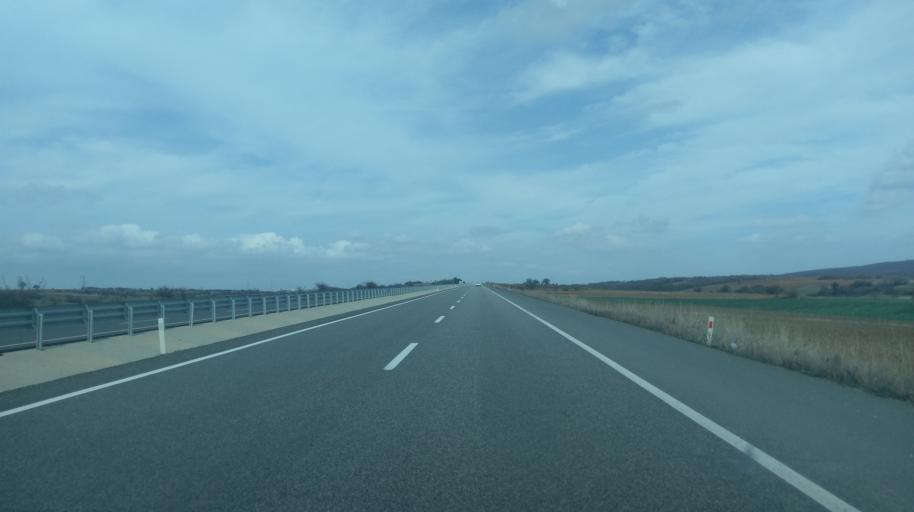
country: TR
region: Edirne
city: Hamidiye
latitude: 41.1178
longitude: 26.6523
